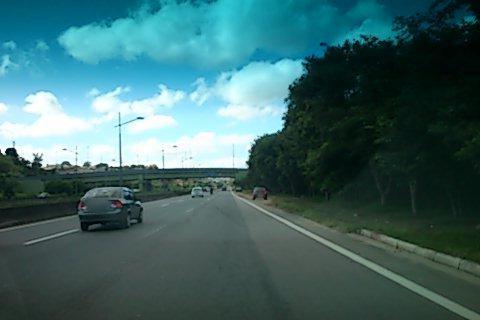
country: BR
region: Sao Paulo
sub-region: Sao Jose Dos Campos
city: Sao Jose dos Campos
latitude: -23.2162
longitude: -45.8873
